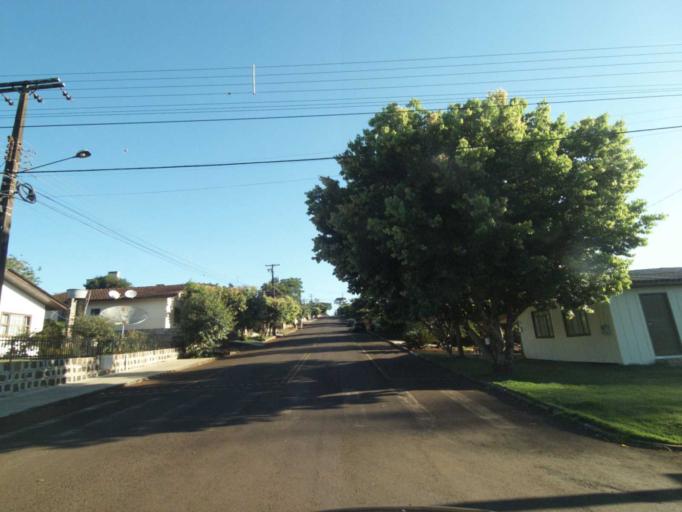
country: BR
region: Parana
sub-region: Coronel Vivida
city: Coronel Vivida
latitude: -25.9659
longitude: -52.8125
